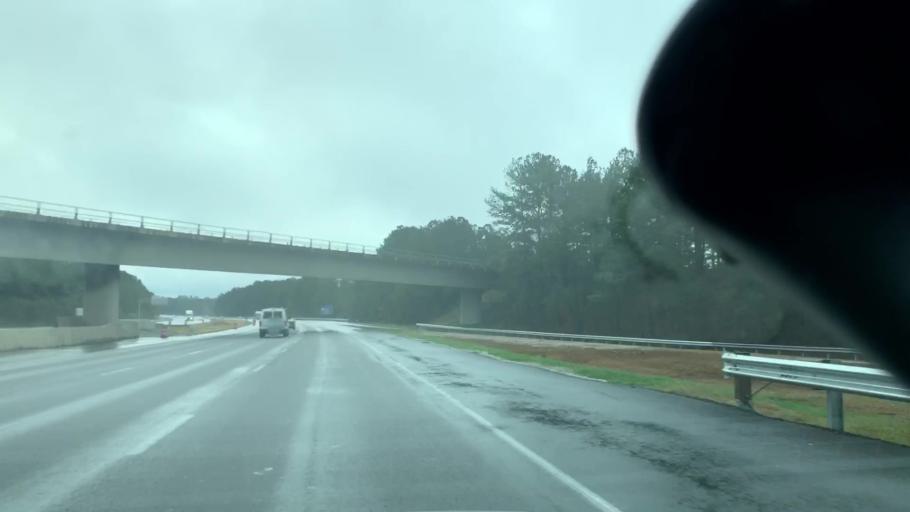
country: US
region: South Carolina
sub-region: Richland County
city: Dentsville
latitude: 34.0939
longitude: -80.9548
